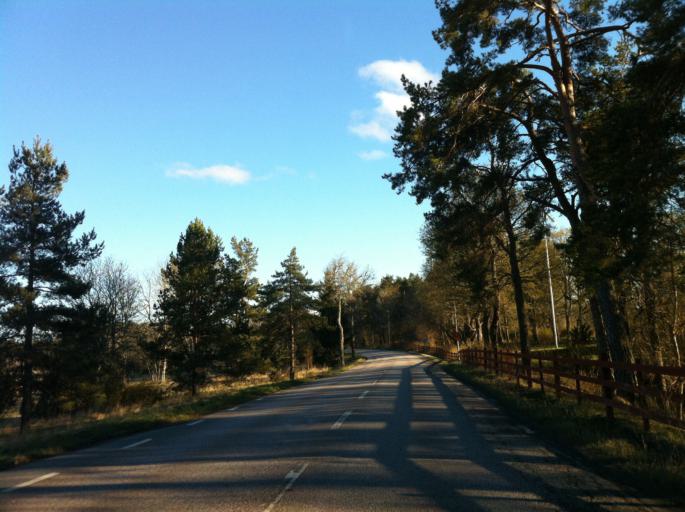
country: SE
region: Uppsala
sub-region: Osthammars Kommun
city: Anneberg
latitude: 60.1826
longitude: 18.3985
